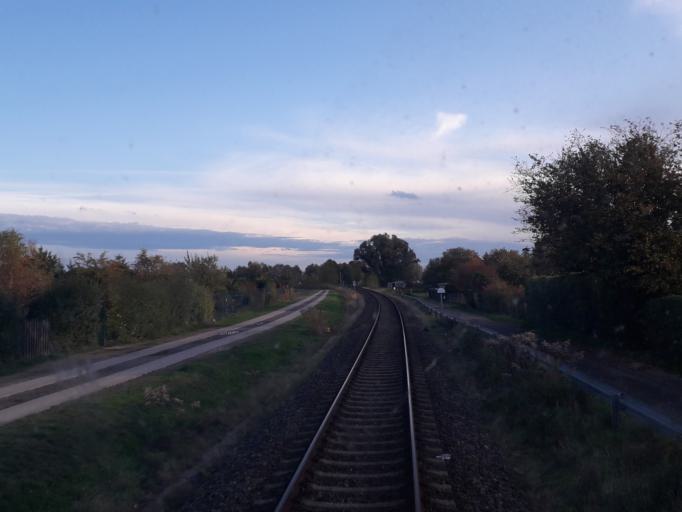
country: DE
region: Brandenburg
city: Wittstock
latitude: 53.1566
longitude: 12.4862
